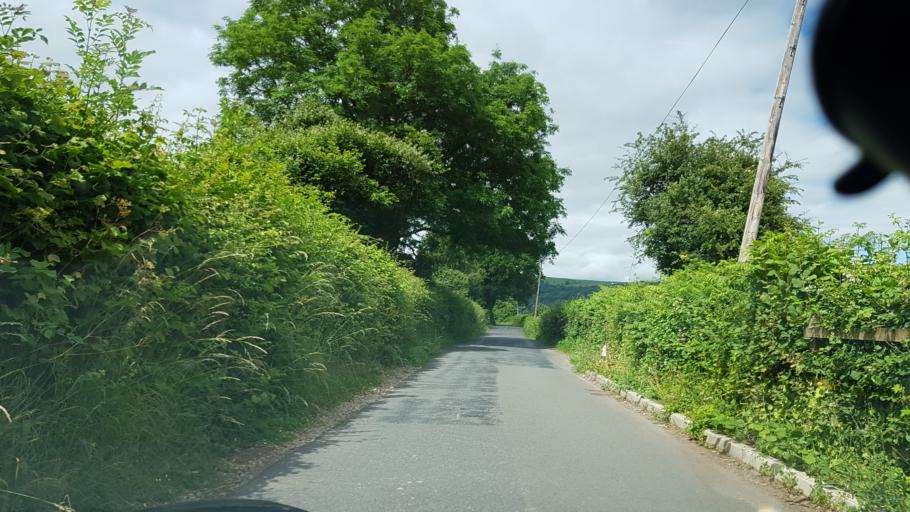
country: GB
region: Wales
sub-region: Monmouthshire
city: Grosmont
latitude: 51.8952
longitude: -2.8288
